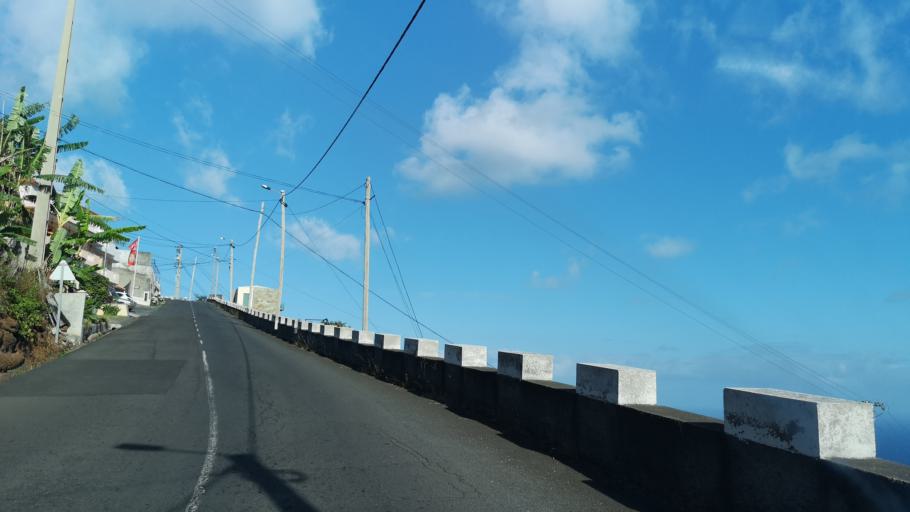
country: PT
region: Madeira
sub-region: Santa Cruz
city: Camacha
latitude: 32.6585
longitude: -16.8384
